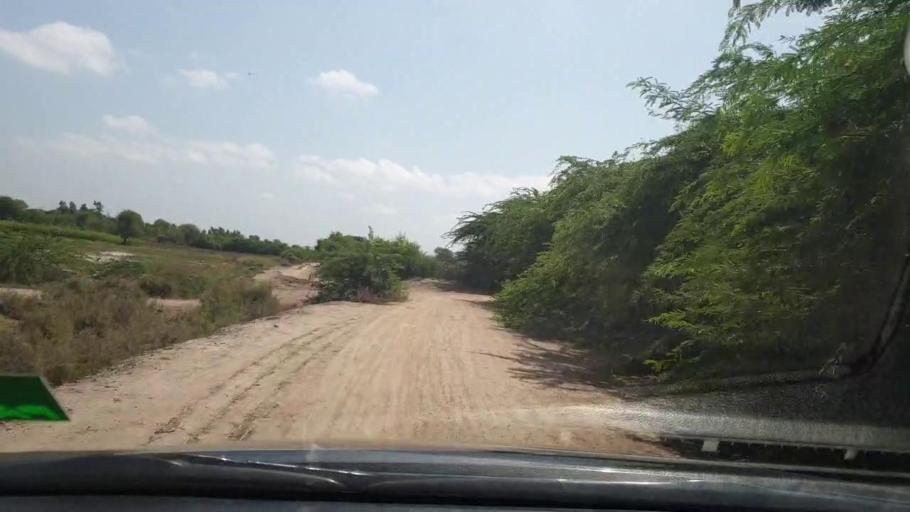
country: PK
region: Sindh
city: Tando Bago
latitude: 24.8529
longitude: 69.0912
